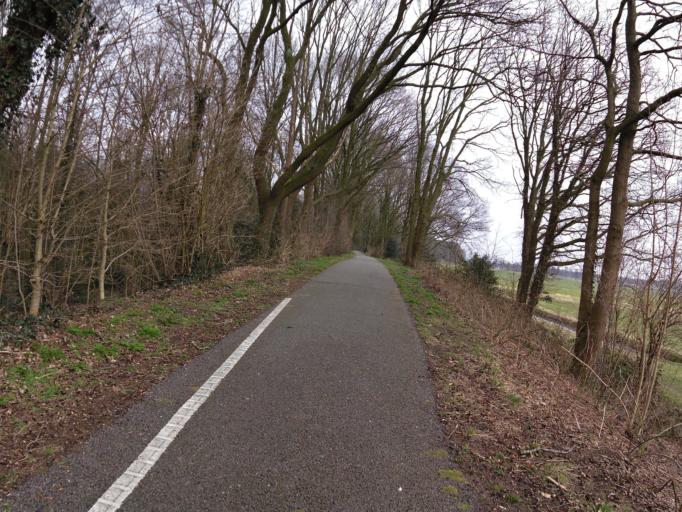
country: NL
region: North Brabant
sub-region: Gemeente Heusden
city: Heusden
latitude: 51.6769
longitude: 5.1310
